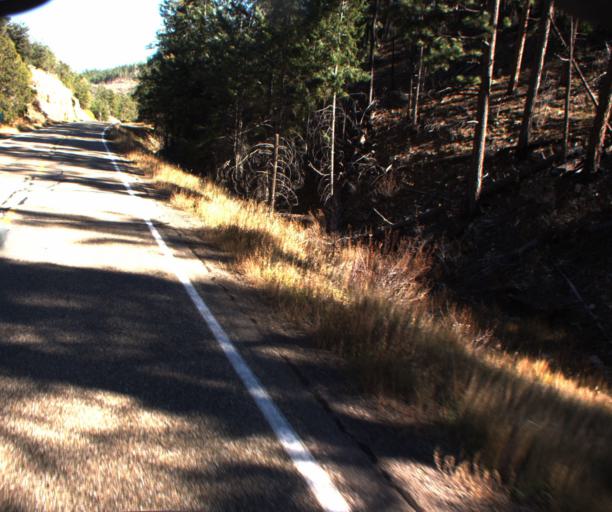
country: US
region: Arizona
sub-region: Coconino County
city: Fredonia
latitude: 36.7320
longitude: -112.1588
